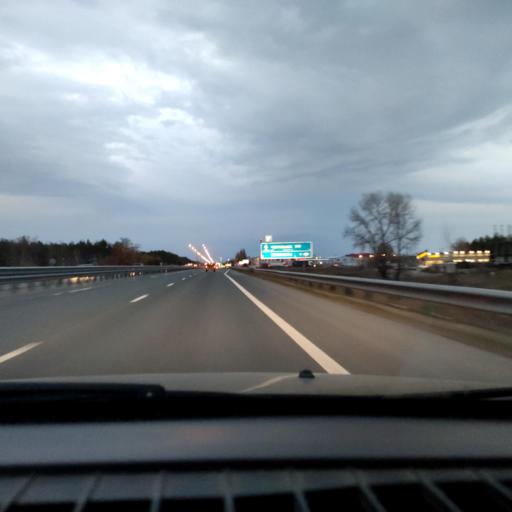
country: RU
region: Samara
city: Zhigulevsk
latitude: 53.5130
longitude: 49.5874
